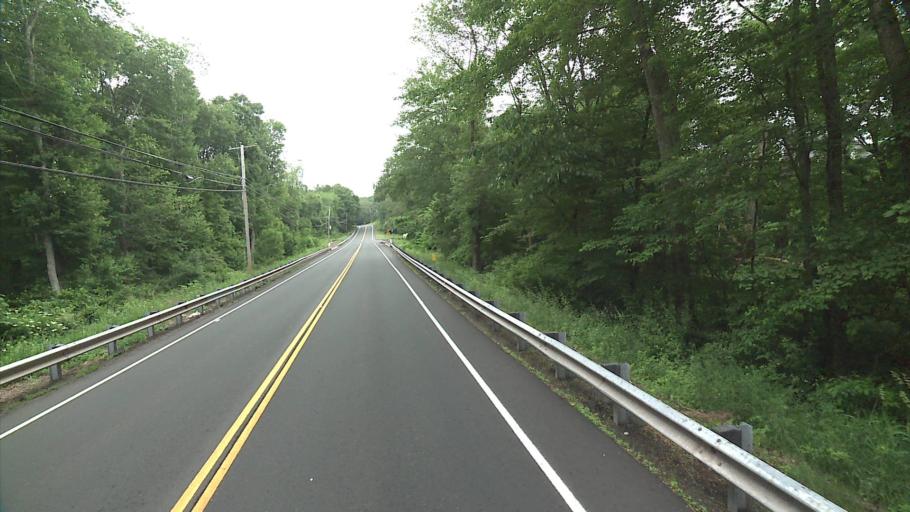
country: US
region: Connecticut
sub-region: Hartford County
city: Manchester
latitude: 41.7098
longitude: -72.5077
